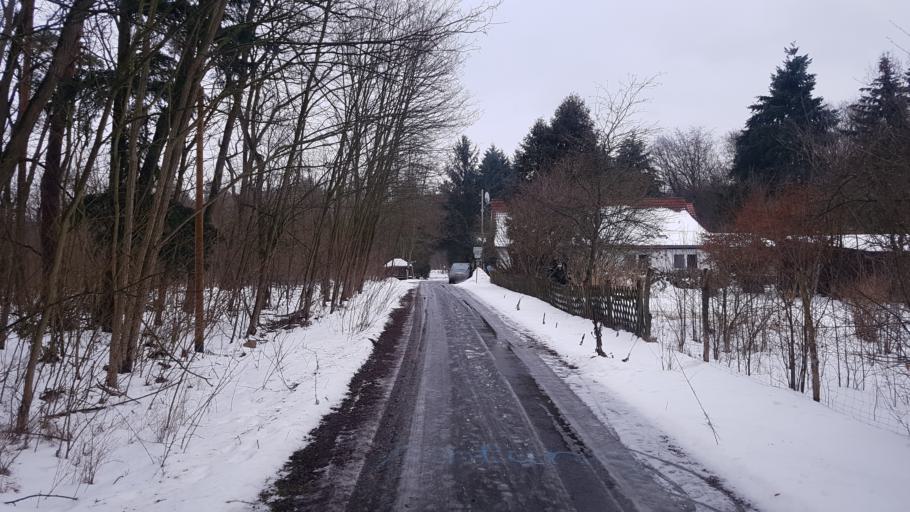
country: DE
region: Brandenburg
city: Bronkow
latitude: 51.6537
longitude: 13.9415
